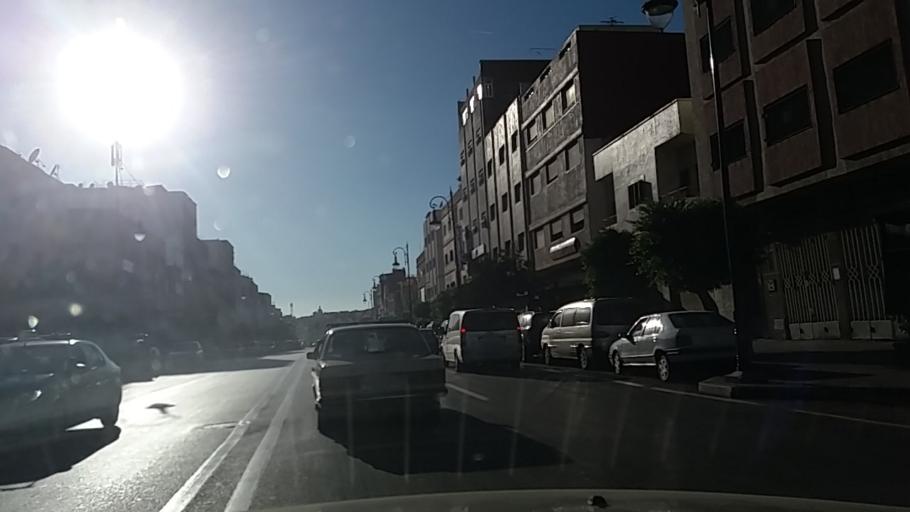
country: MA
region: Tanger-Tetouan
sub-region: Tanger-Assilah
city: Tangier
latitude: 35.7527
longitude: -5.8069
